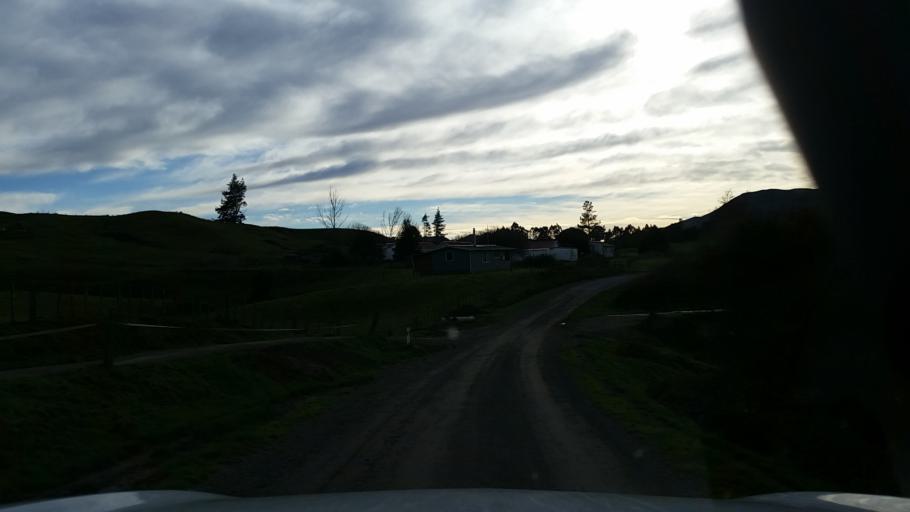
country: NZ
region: Bay of Plenty
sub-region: Rotorua District
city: Rotorua
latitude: -38.2666
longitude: 176.1569
